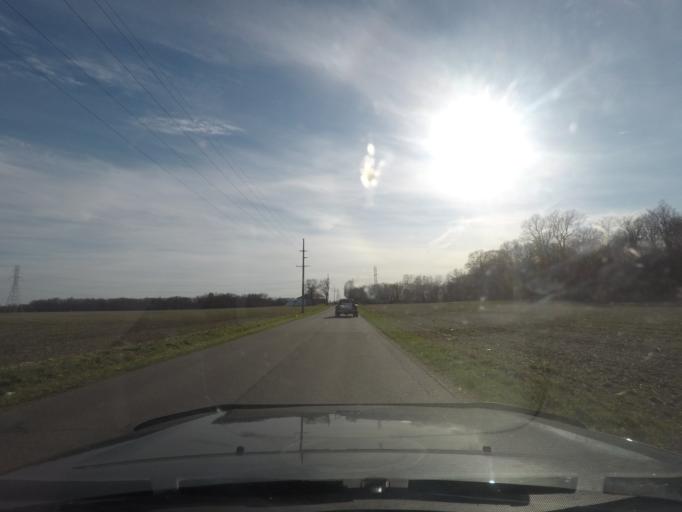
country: US
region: Indiana
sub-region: Marshall County
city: Bremen
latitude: 41.4565
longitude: -86.0889
